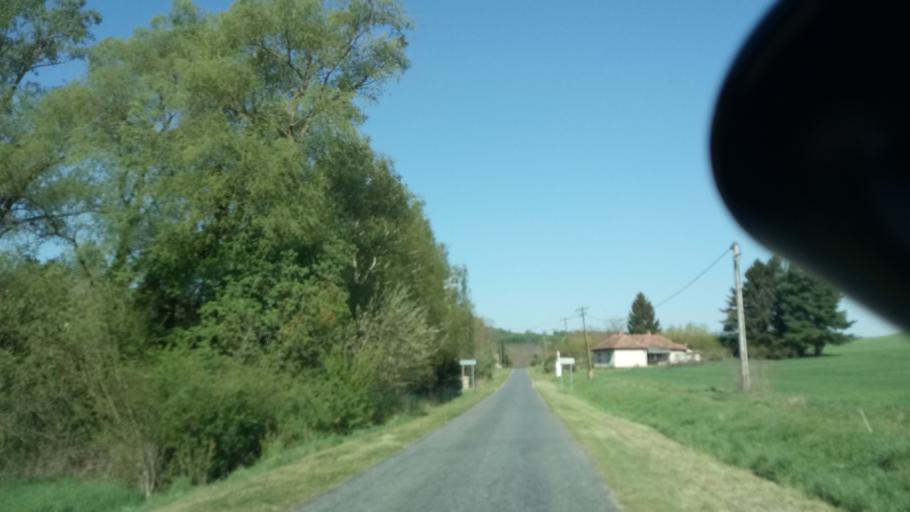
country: HU
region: Zala
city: Pacsa
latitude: 46.6898
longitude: 17.0891
